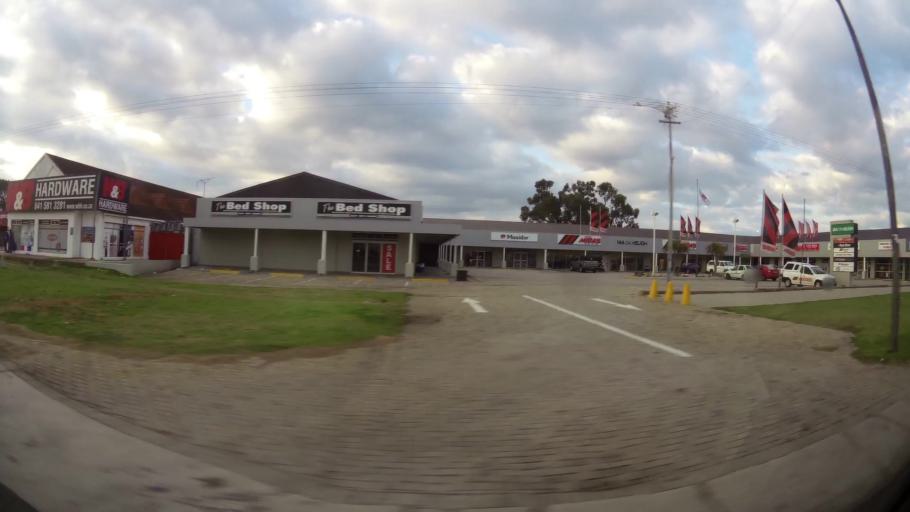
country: ZA
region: Eastern Cape
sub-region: Nelson Mandela Bay Metropolitan Municipality
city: Port Elizabeth
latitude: -33.9813
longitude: 25.5952
